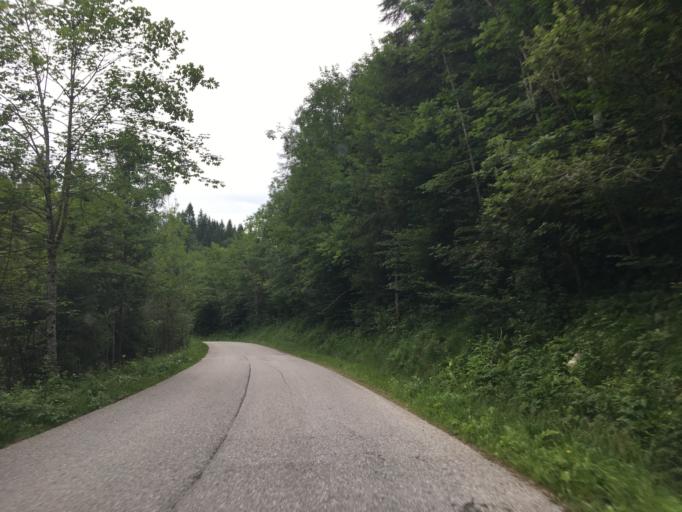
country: AT
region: Salzburg
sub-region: Politischer Bezirk Salzburg-Umgebung
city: Strobl
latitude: 47.6905
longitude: 13.4850
